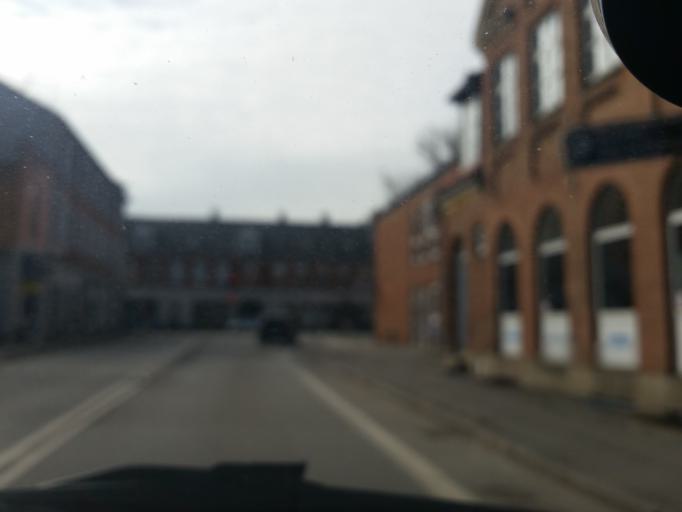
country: DK
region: Zealand
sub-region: Soro Kommune
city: Soro
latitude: 55.4346
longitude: 11.5587
